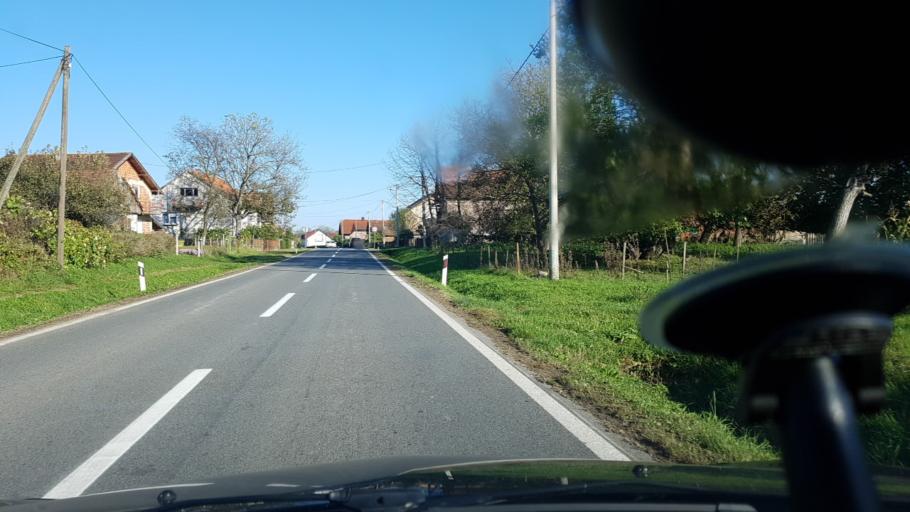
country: HR
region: Bjelovarsko-Bilogorska
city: Gudovac
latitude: 45.8323
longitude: 16.7949
